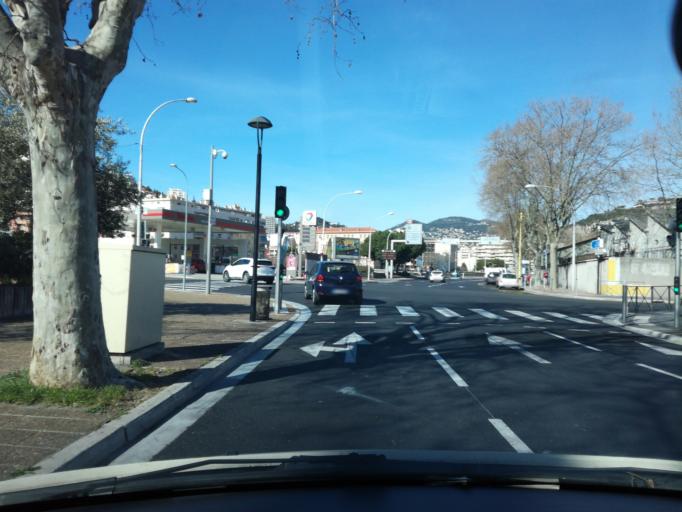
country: FR
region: Provence-Alpes-Cote d'Azur
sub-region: Departement des Alpes-Maritimes
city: Saint-Andre-de-la-Roche
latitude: 43.7161
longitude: 7.2826
